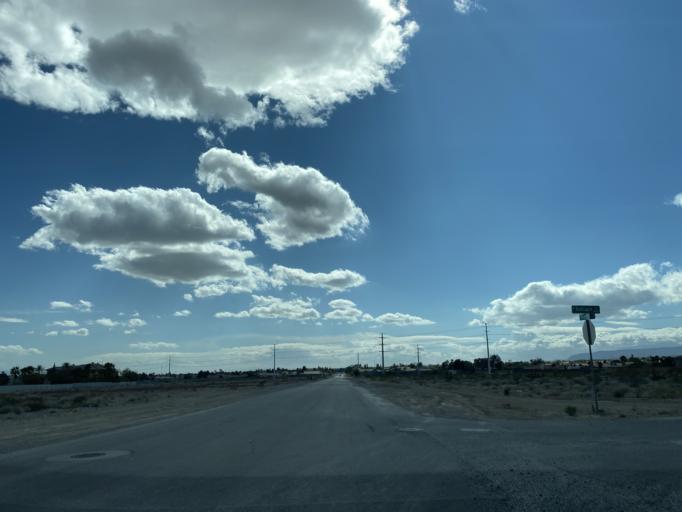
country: US
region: Nevada
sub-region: Clark County
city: Summerlin South
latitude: 36.2449
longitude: -115.2884
